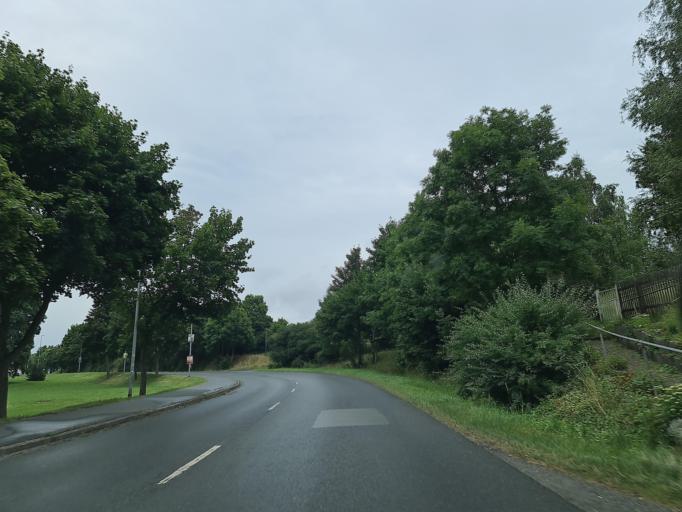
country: DE
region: Saxony
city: Oelsnitz
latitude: 50.4248
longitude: 12.1761
